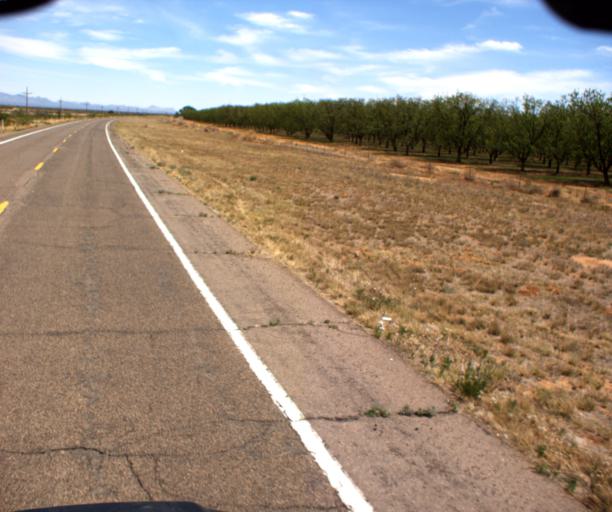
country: US
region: Arizona
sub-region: Cochise County
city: Willcox
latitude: 32.3251
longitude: -109.4756
